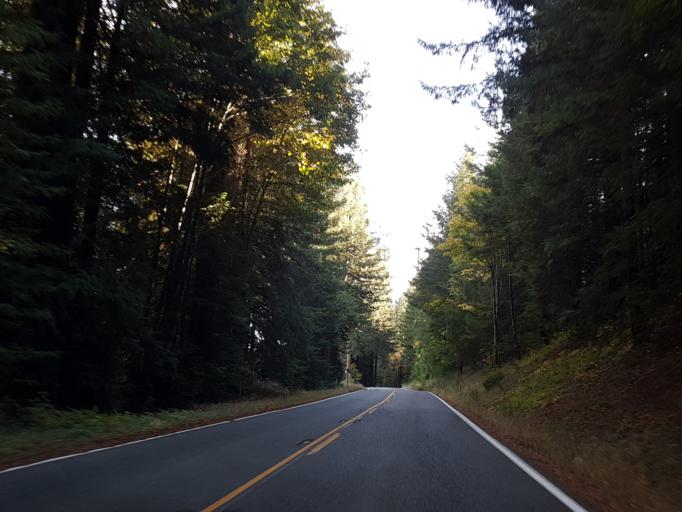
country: US
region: California
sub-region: Humboldt County
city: Rio Dell
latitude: 40.4299
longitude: -123.9840
